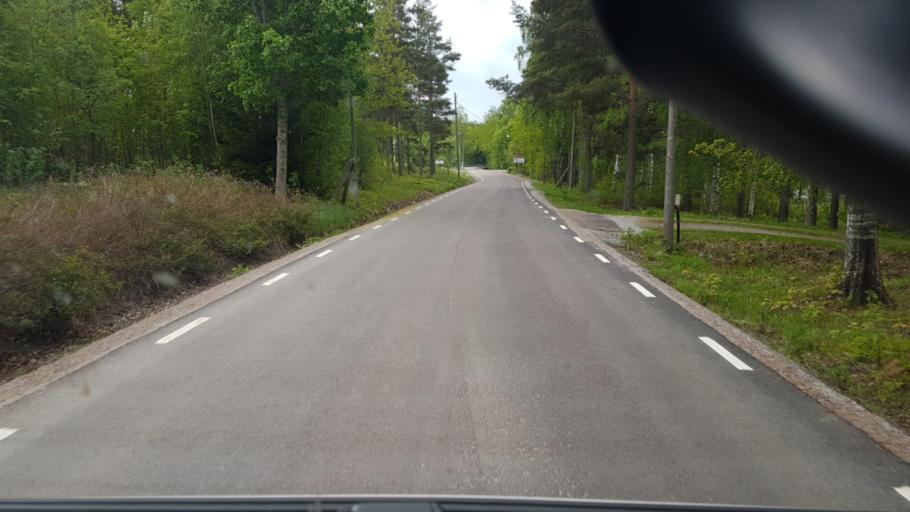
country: SE
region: Vaermland
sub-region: Arvika Kommun
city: Arvika
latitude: 59.5322
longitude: 12.7420
